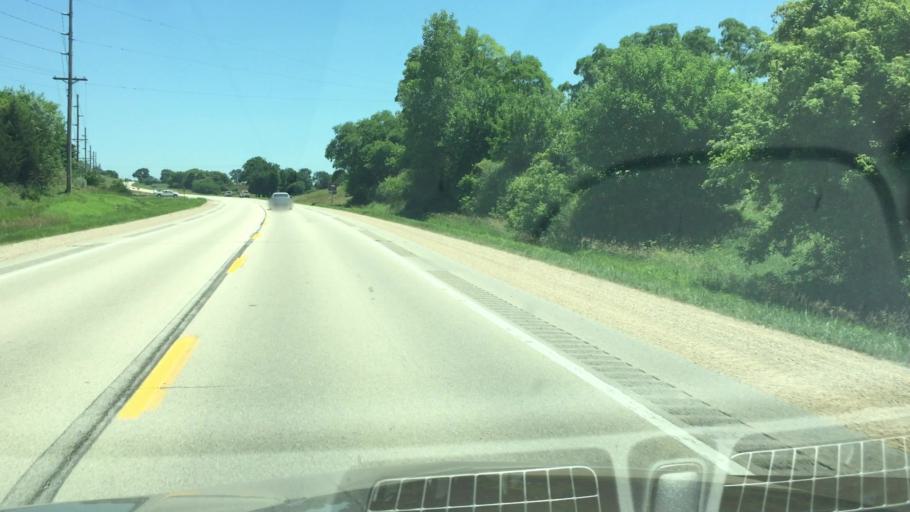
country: US
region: Iowa
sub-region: Jackson County
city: Maquoketa
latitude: 42.0624
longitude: -90.7592
